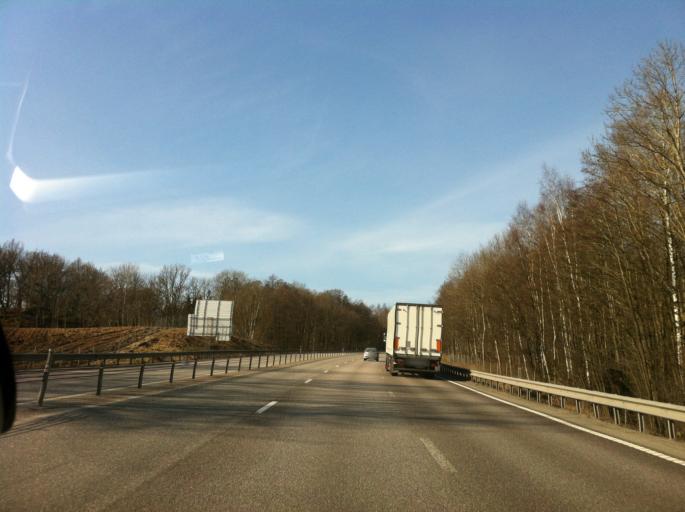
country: SE
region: Joenkoeping
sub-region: Jonkopings Kommun
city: Jonkoping
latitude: 57.7495
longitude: 14.1231
